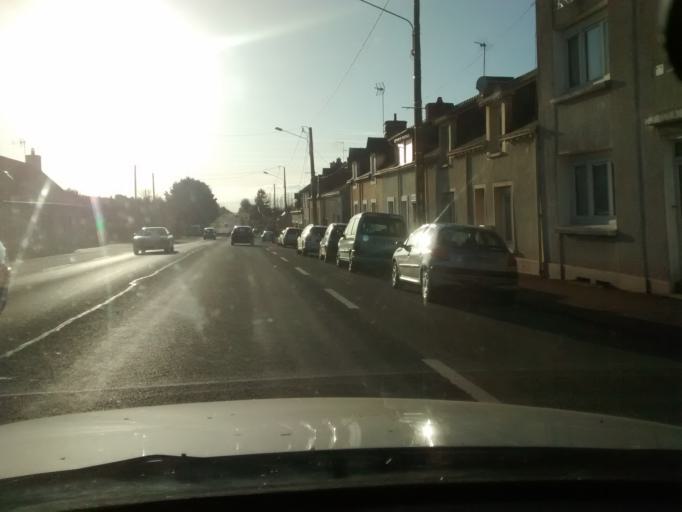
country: FR
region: Pays de la Loire
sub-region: Departement de la Sarthe
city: Trange
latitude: 48.0226
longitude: 0.0975
